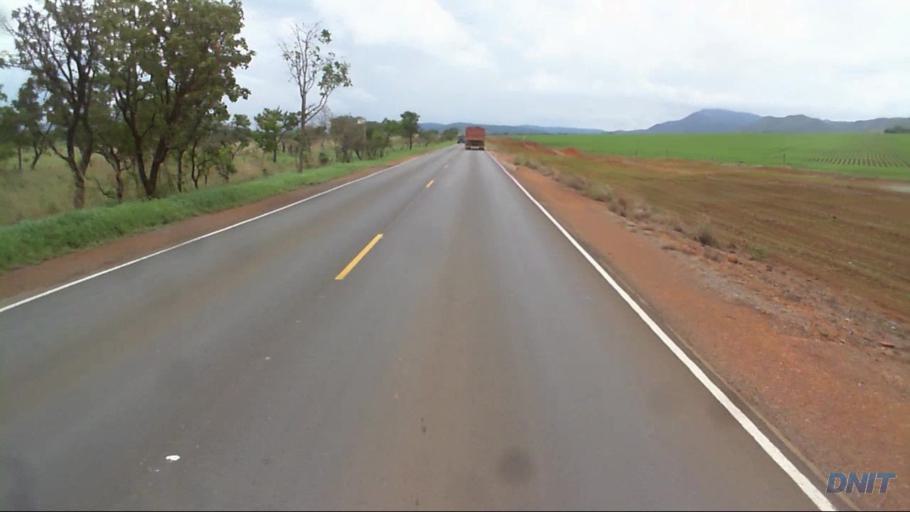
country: BR
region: Goias
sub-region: Padre Bernardo
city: Padre Bernardo
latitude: -15.3333
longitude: -48.2328
